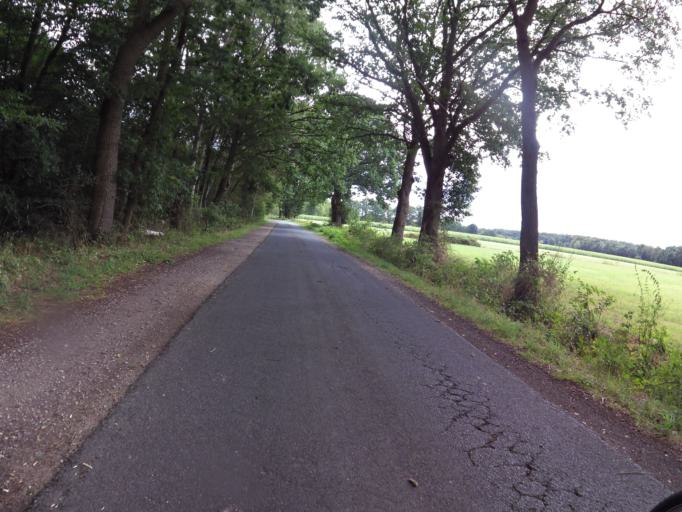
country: DE
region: Lower Saxony
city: Schiffdorf
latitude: 53.5034
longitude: 8.6976
